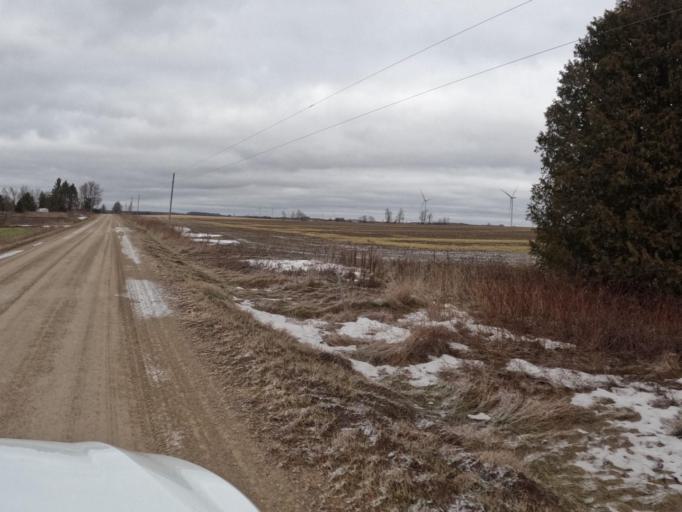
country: CA
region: Ontario
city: Shelburne
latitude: 44.0236
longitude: -80.3694
